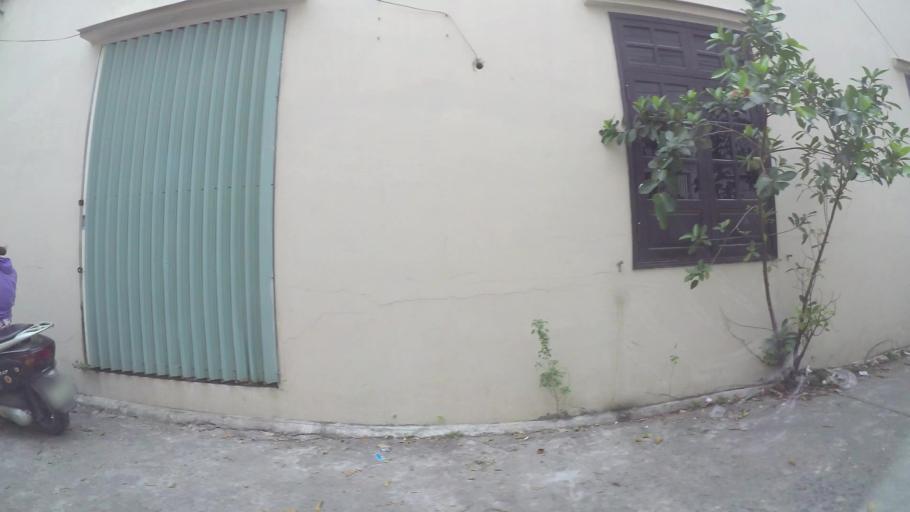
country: VN
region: Da Nang
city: Thanh Khe
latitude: 16.0493
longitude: 108.1843
